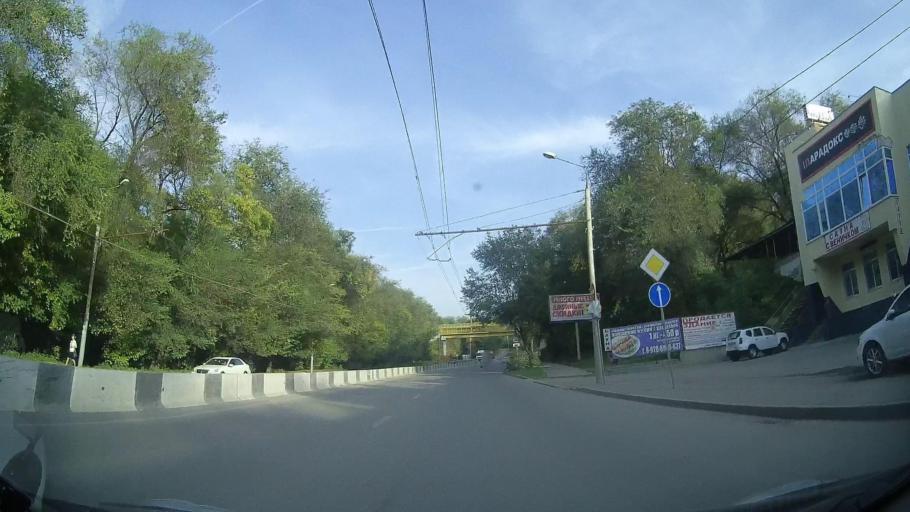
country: RU
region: Rostov
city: Temernik
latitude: 47.2904
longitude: 39.7358
